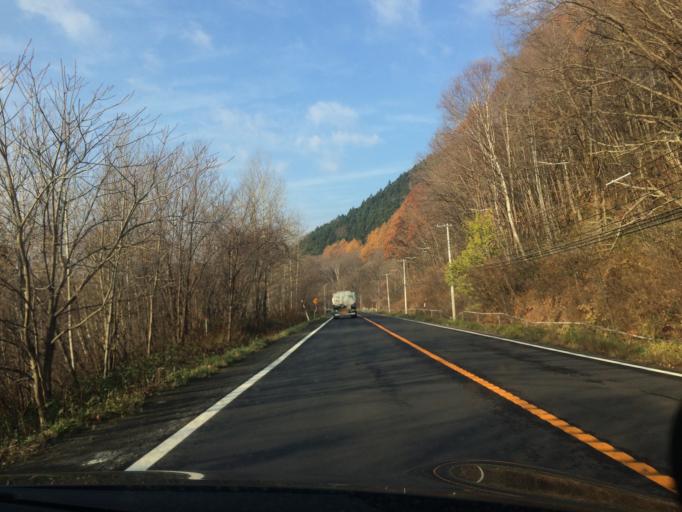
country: JP
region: Hokkaido
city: Shimo-furano
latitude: 42.8956
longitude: 142.4835
